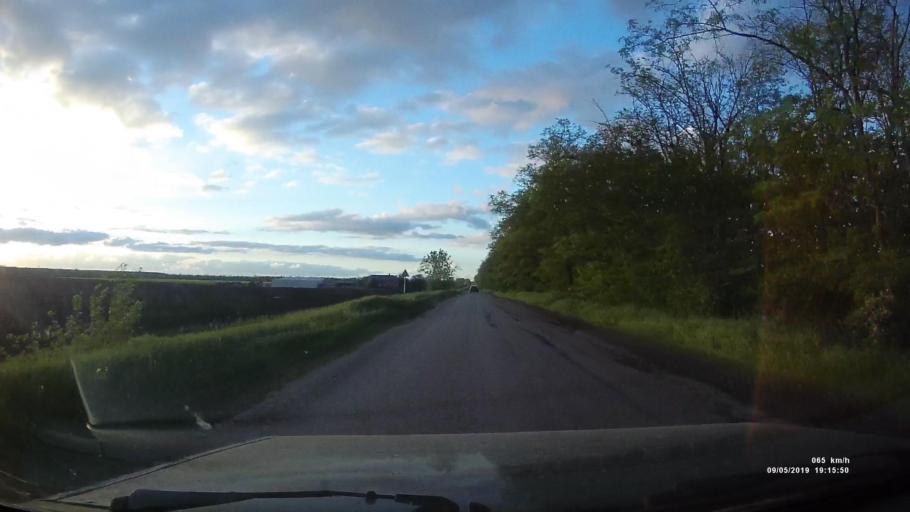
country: RU
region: Krasnodarskiy
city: Kanelovskaya
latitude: 46.7722
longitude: 39.2114
